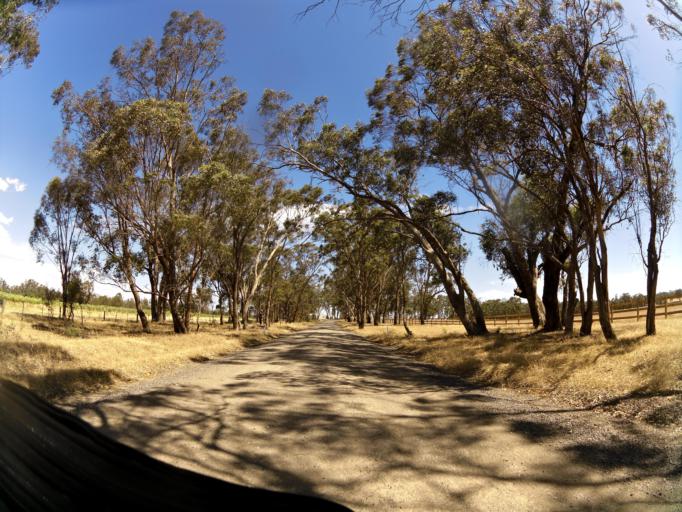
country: AU
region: Victoria
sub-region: Campaspe
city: Kyabram
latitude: -36.8369
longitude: 145.0743
